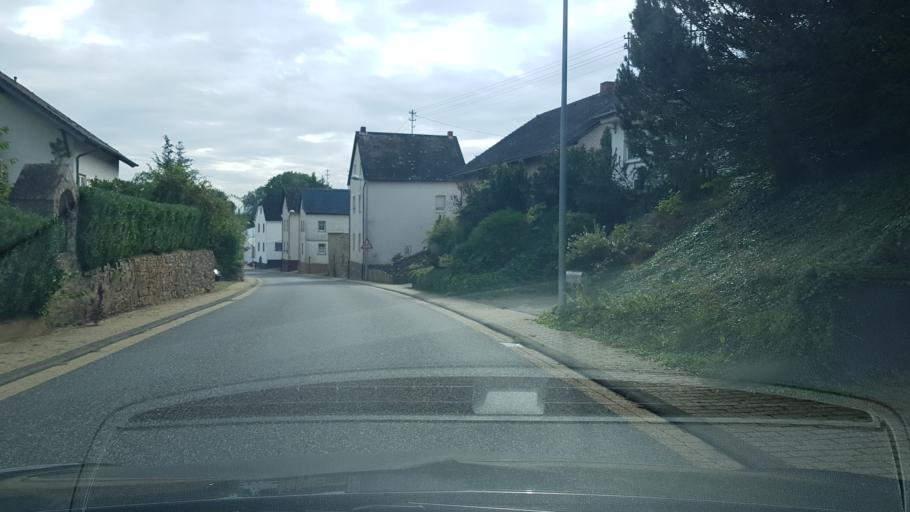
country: DE
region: Rheinland-Pfalz
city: Munstermaifeld
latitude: 50.2393
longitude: 7.3794
